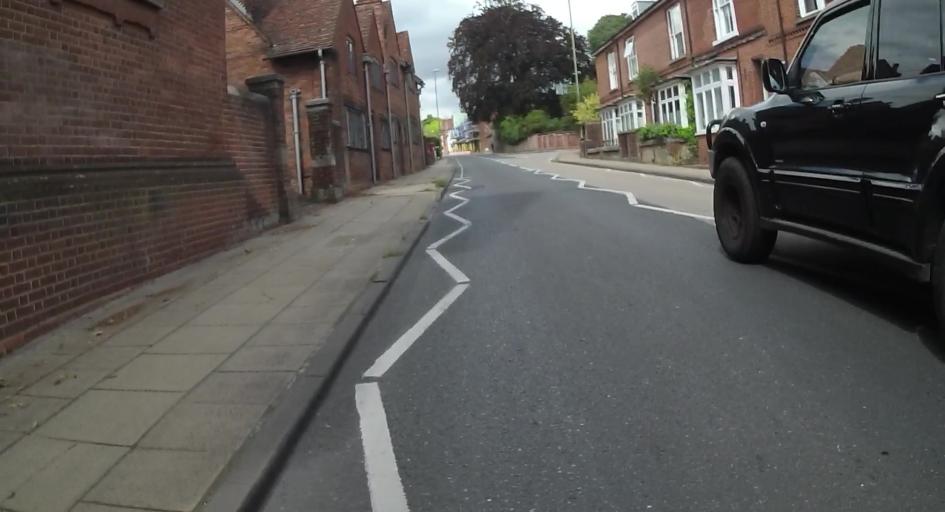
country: GB
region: England
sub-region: Hampshire
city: Winchester
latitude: 51.0584
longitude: -1.3190
